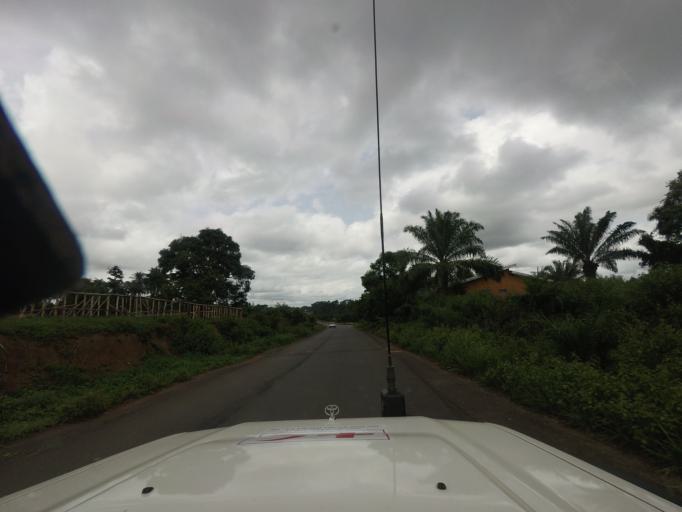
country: GN
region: Nzerekore
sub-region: Macenta
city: Macenta
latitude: 8.2834
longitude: -9.1782
